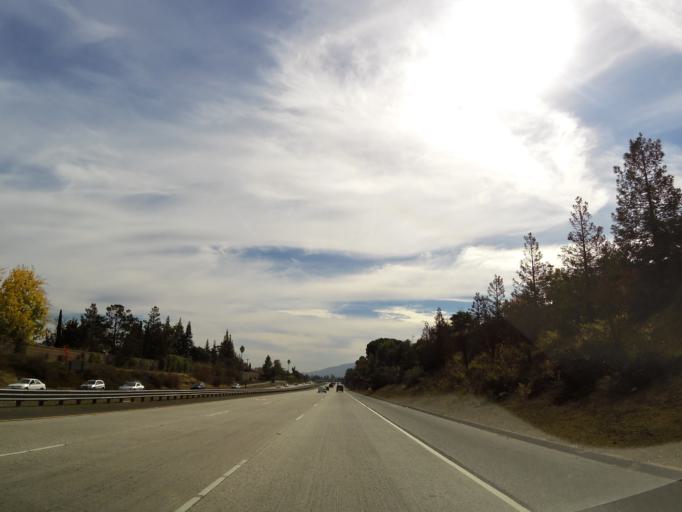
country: US
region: California
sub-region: Santa Clara County
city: Cupertino
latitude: 37.3085
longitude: -122.0414
